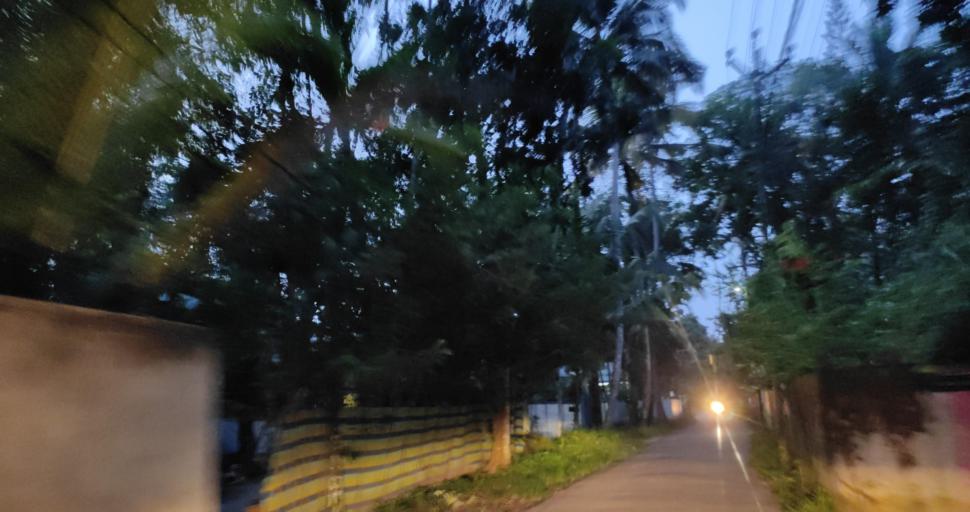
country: IN
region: Kerala
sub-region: Alappuzha
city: Vayalar
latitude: 9.7170
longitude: 76.2919
